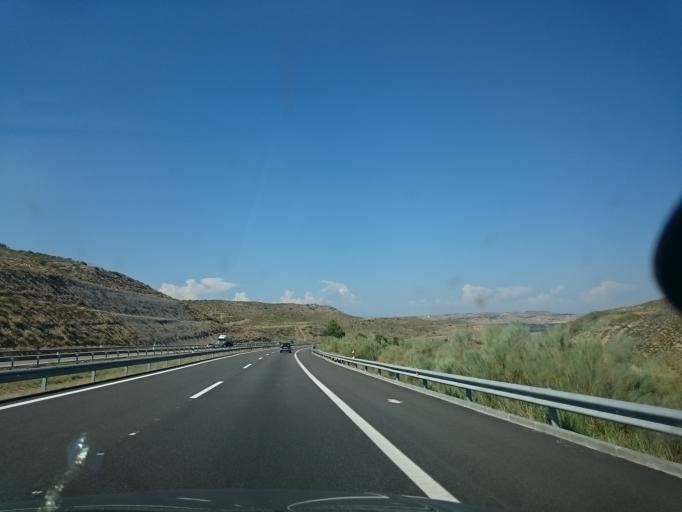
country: ES
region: Aragon
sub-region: Provincia de Huesca
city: Fraga
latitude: 41.4772
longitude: 0.3143
